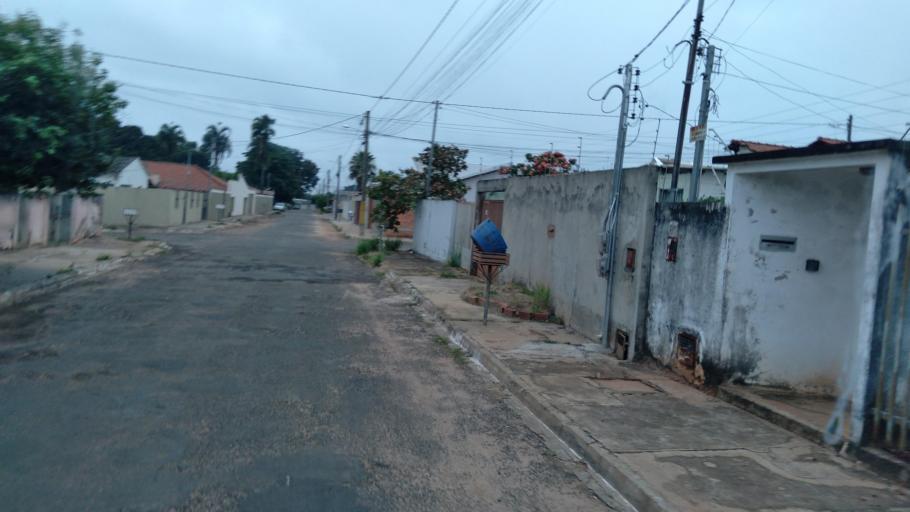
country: BR
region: Goias
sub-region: Mineiros
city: Mineiros
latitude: -17.5802
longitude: -52.5461
